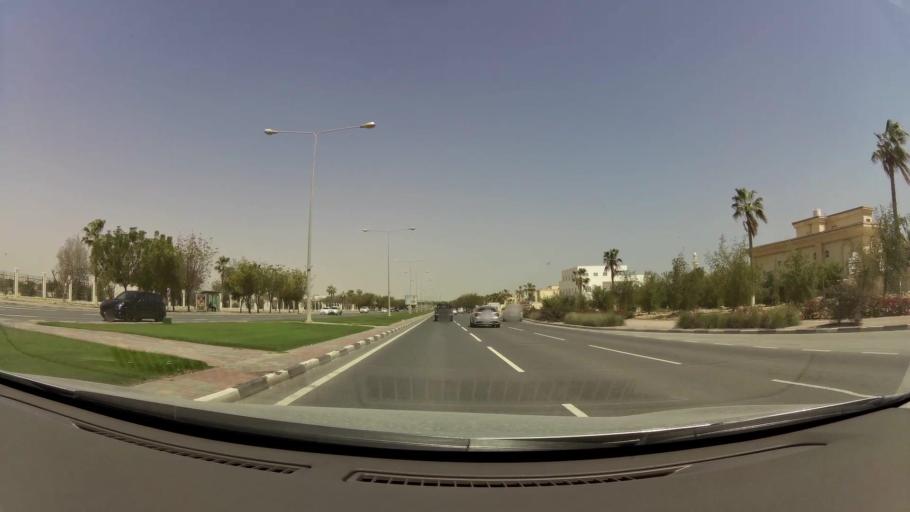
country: QA
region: Baladiyat ad Dawhah
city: Doha
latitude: 25.3592
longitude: 51.4952
